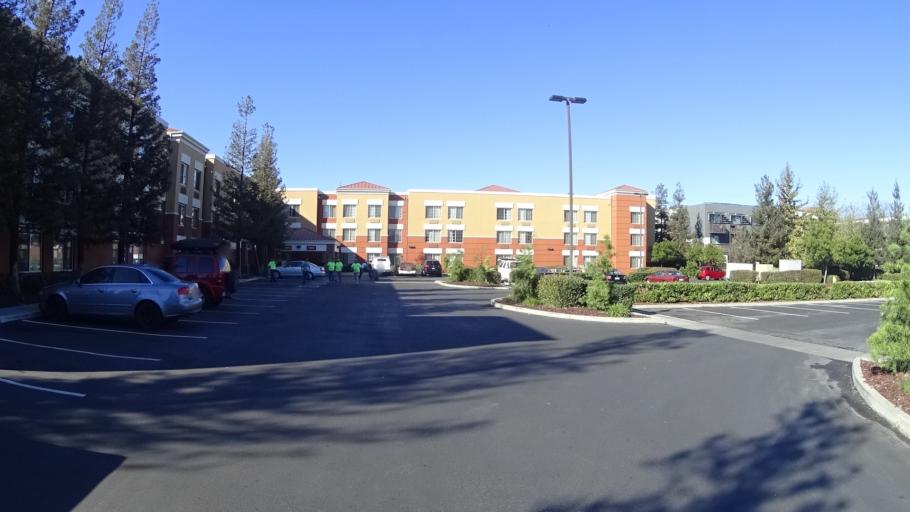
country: US
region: California
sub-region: Santa Clara County
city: San Jose
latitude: 37.3645
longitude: -121.9109
